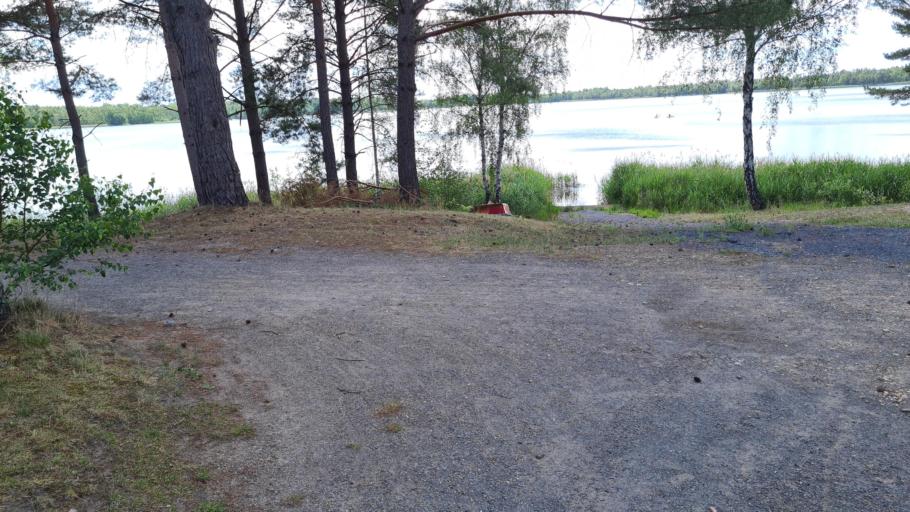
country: DE
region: Brandenburg
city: Plessa
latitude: 51.5186
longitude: 13.6558
